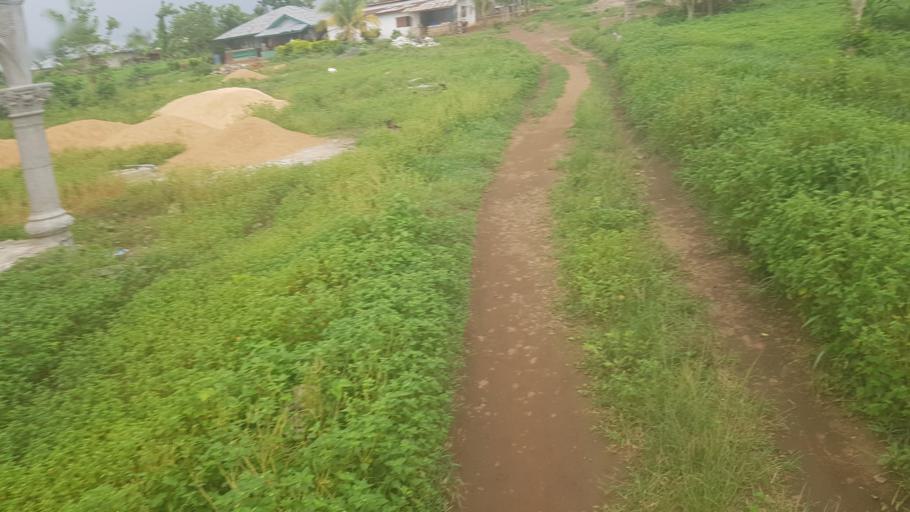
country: SL
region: Southern Province
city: Mogbwemo
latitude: 7.6139
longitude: -12.1752
